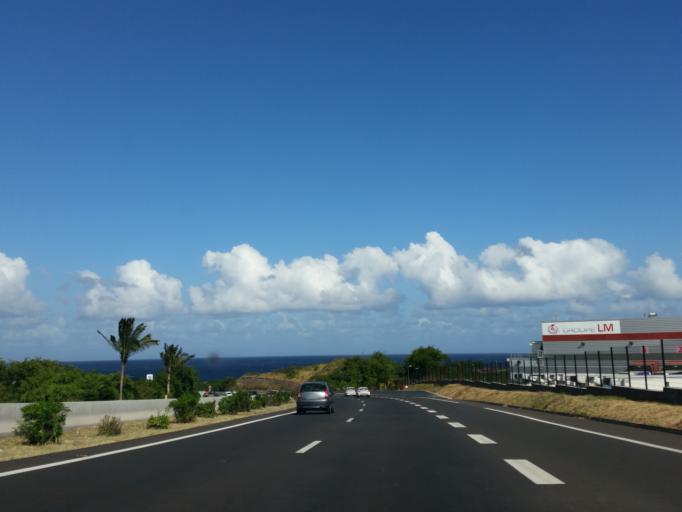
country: RE
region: Reunion
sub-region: Reunion
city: Saint-Pierre
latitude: -21.3220
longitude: 55.4462
